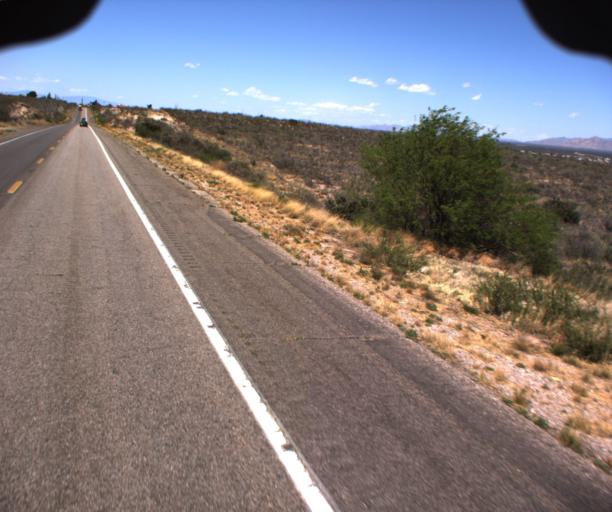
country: US
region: Arizona
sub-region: Cochise County
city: Tombstone
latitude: 31.7010
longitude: -110.0480
